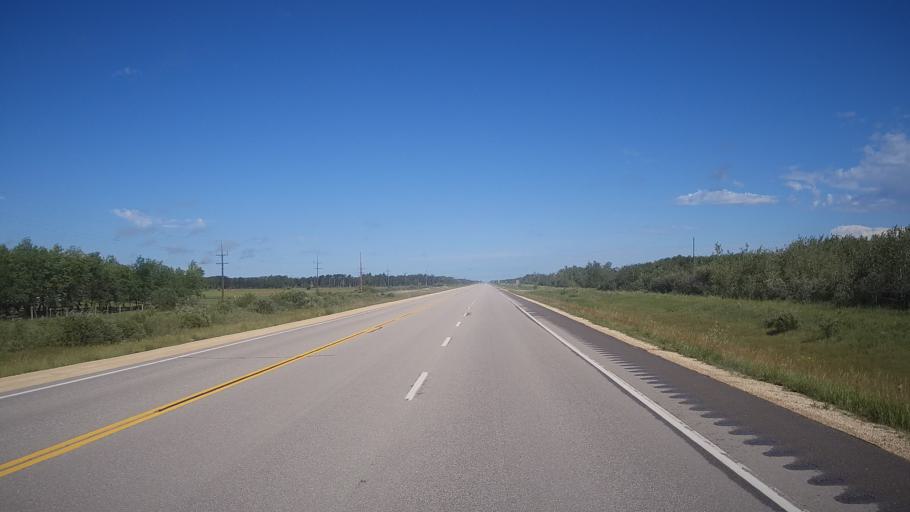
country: CA
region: Manitoba
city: Stonewall
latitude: 50.2270
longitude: -97.6929
